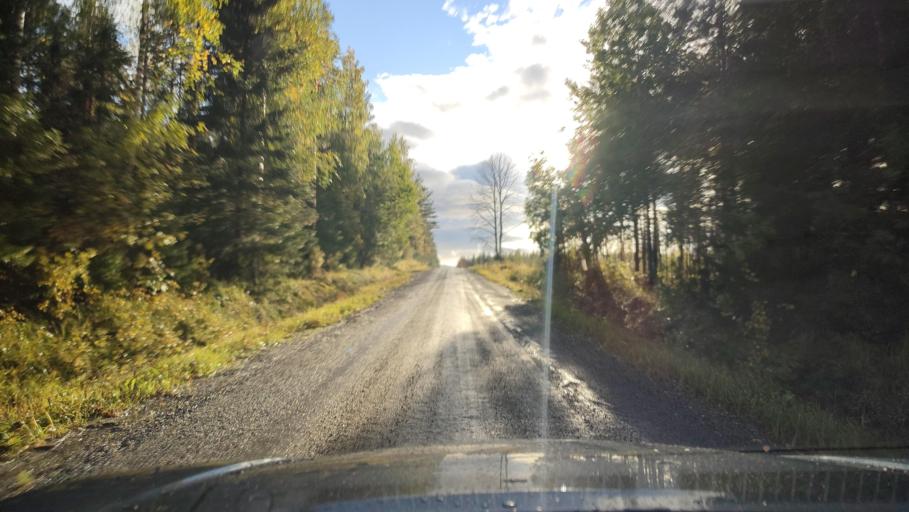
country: FI
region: Southern Ostrobothnia
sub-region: Suupohja
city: Karijoki
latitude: 62.3086
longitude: 21.5434
